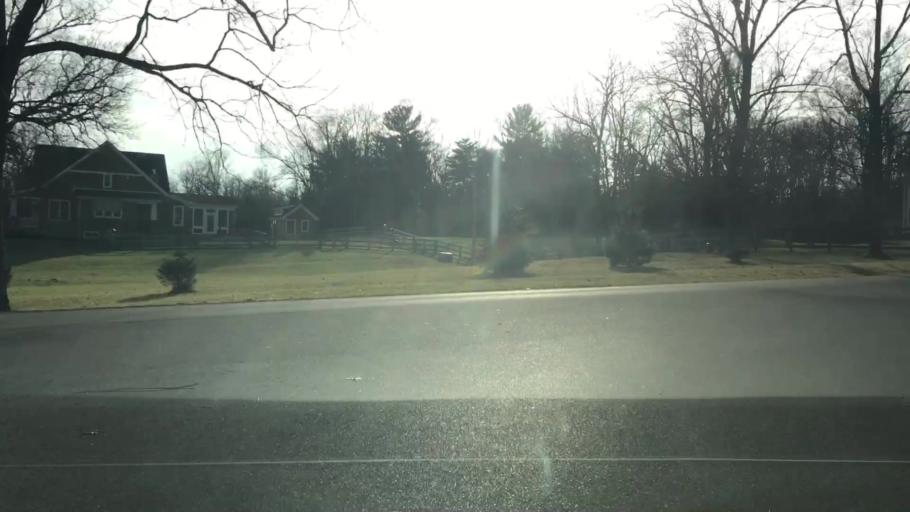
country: US
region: Ohio
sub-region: Greene County
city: Yellow Springs
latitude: 39.7933
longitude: -83.8834
